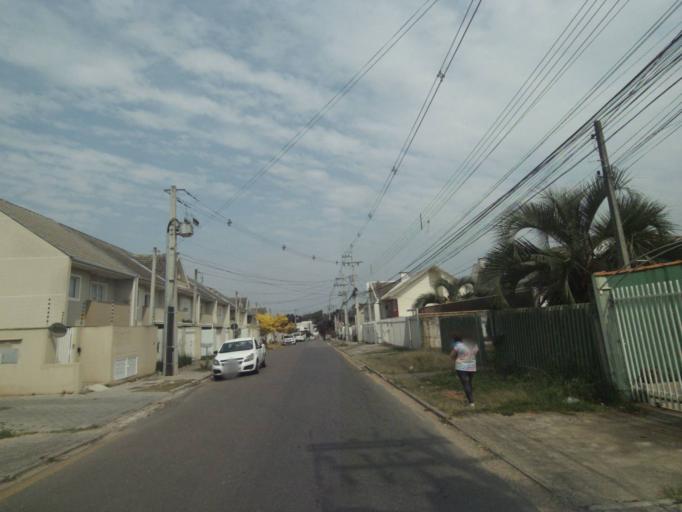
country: BR
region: Parana
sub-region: Pinhais
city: Pinhais
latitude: -25.4735
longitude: -49.2155
